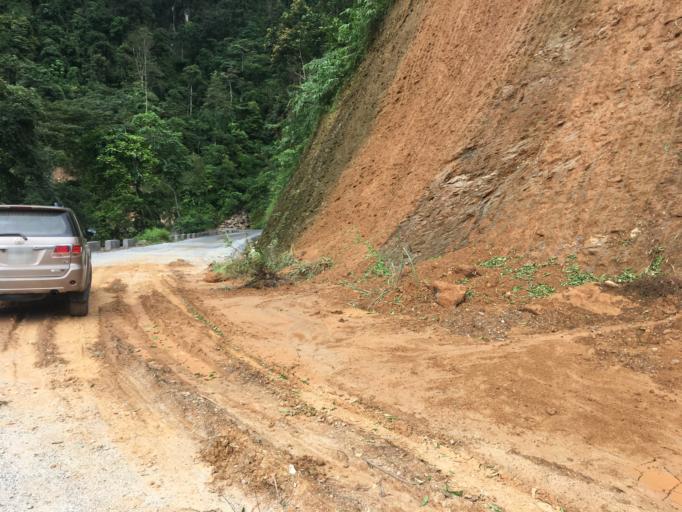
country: VN
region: Ha Giang
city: Thi Tran Tam Son
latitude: 22.9813
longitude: 105.0589
